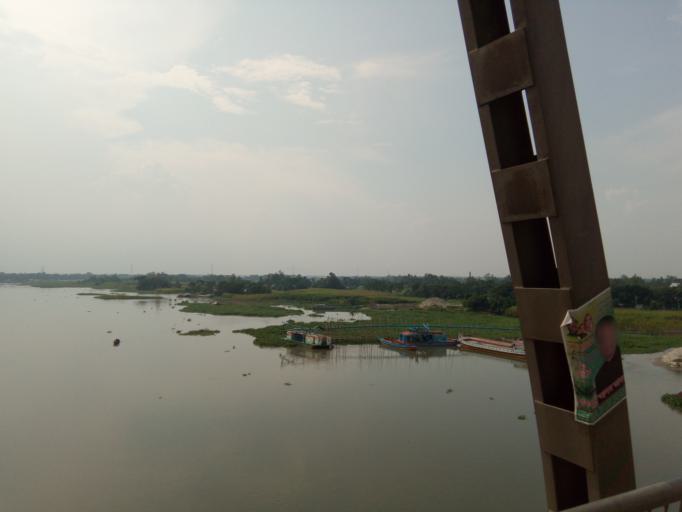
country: BD
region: Dhaka
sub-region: Dhaka
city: Dhaka
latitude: 23.6368
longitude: 90.3462
